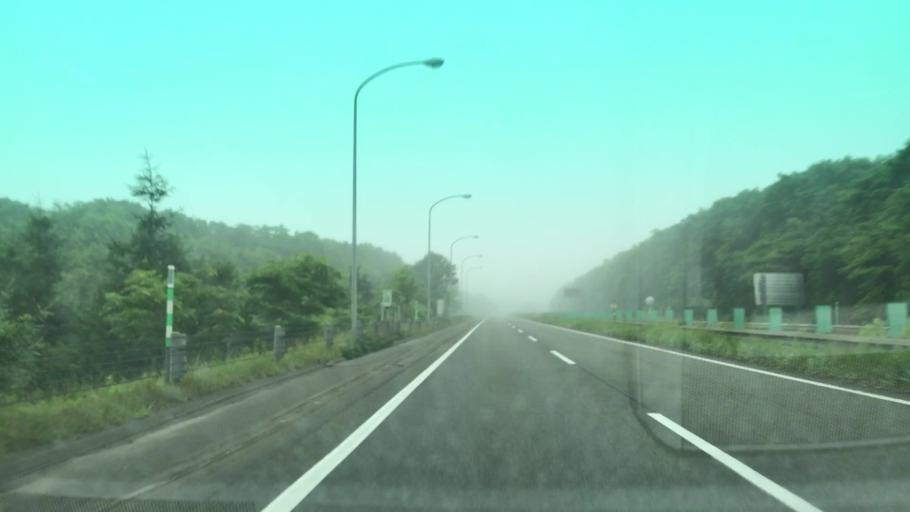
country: JP
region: Hokkaido
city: Chitose
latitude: 42.8050
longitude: 141.6240
